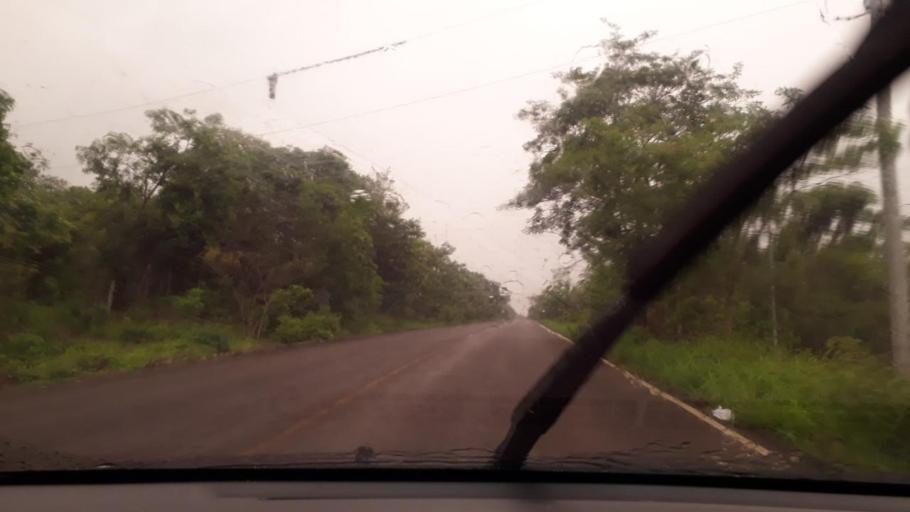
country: GT
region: Jutiapa
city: Comapa
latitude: 14.0800
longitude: -89.9562
